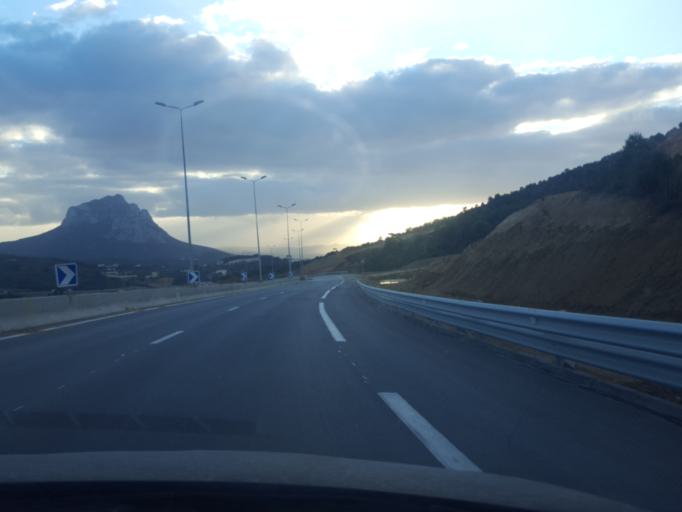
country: TN
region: Tunis
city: Hammam-Lif
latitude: 36.6529
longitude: 10.3713
